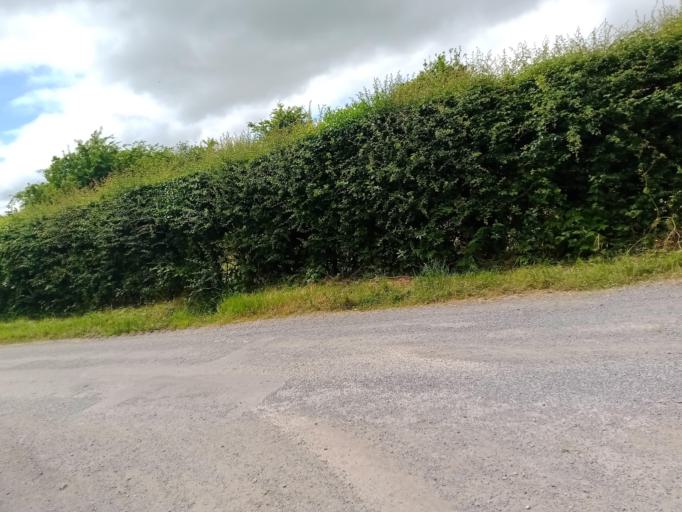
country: IE
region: Leinster
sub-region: Laois
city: Rathdowney
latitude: 52.7940
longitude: -7.4792
